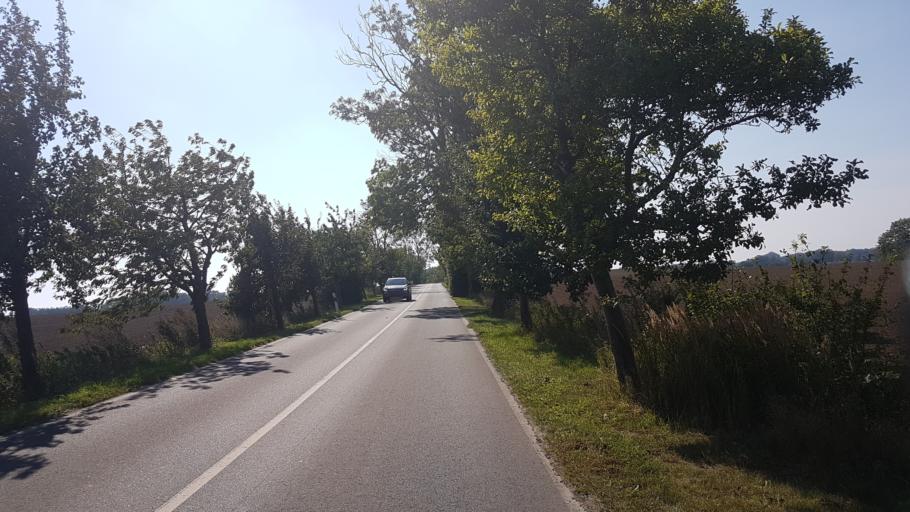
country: DE
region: Mecklenburg-Vorpommern
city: Putbus
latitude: 54.3518
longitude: 13.5097
